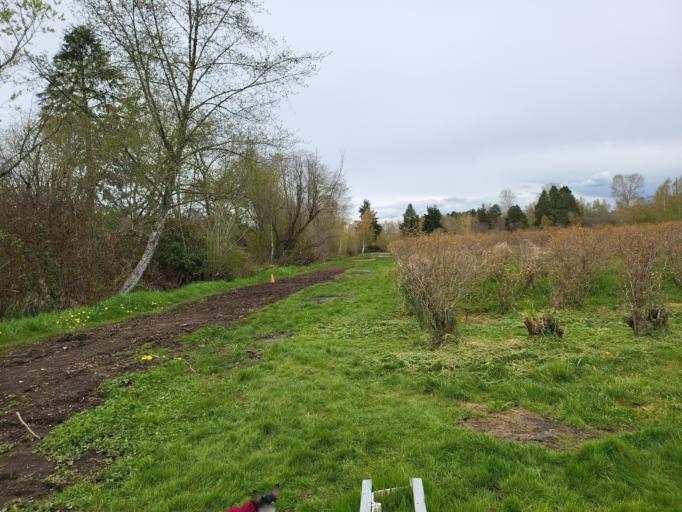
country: US
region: Washington
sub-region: King County
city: Bellevue
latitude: 47.5912
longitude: -122.1911
